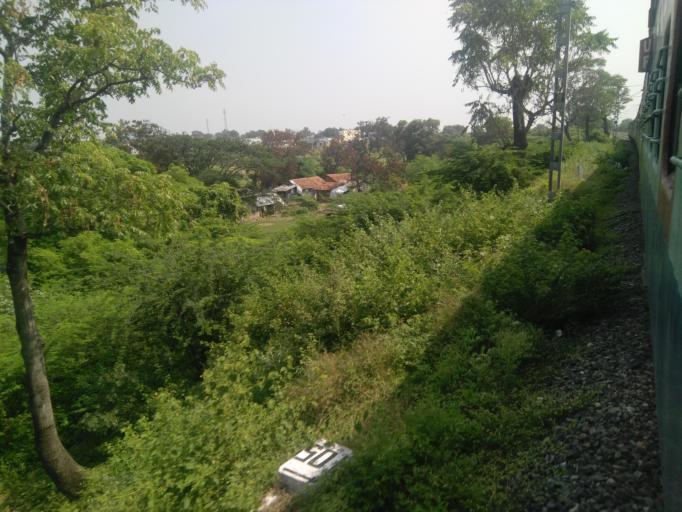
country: IN
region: Tamil Nadu
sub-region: Coimbatore
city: Mettupalayam
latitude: 11.2790
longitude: 76.9414
